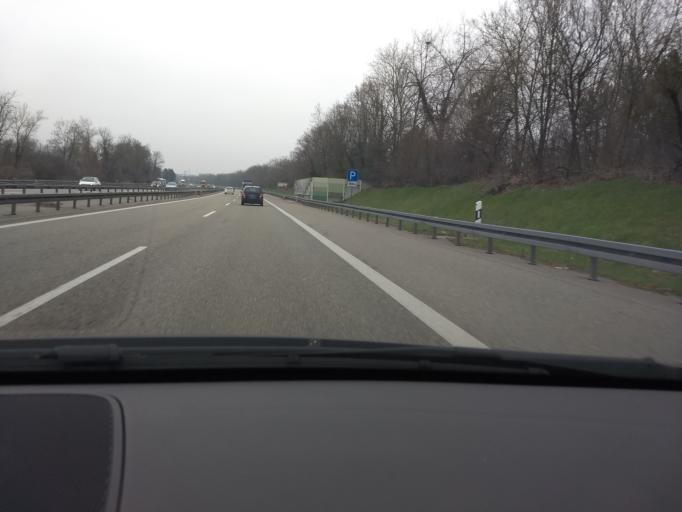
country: DE
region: Baden-Wuerttemberg
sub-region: Freiburg Region
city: Bad Bellingen
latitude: 47.7335
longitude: 7.5517
